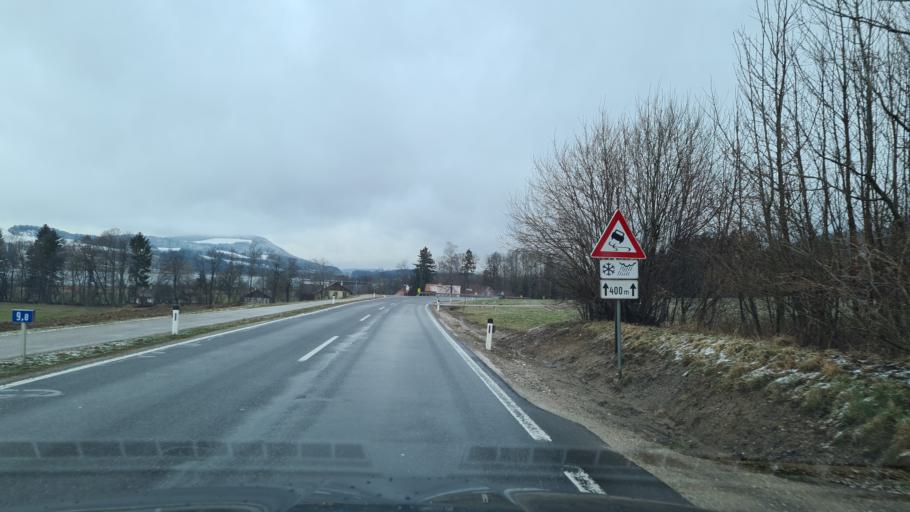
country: AT
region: Upper Austria
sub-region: Politischer Bezirk Vocklabruck
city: Zell am Moos
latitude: 47.9129
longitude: 13.3156
